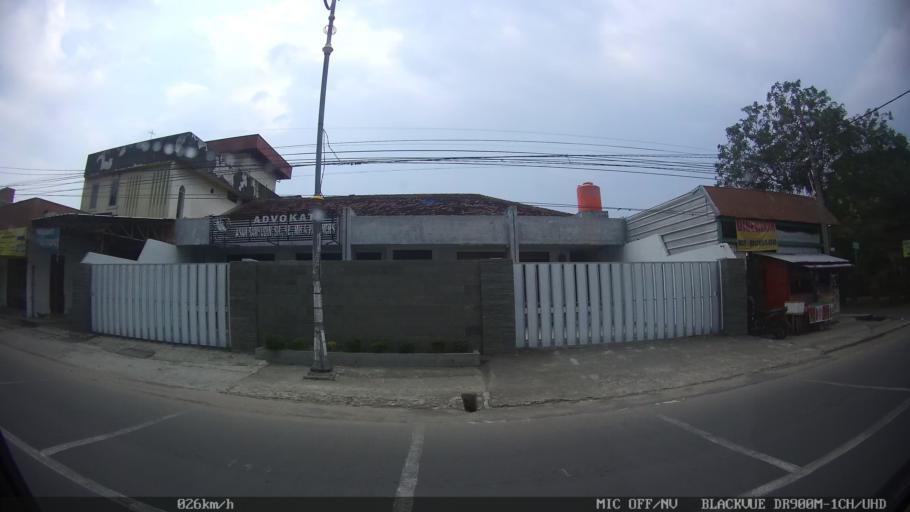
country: ID
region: Lampung
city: Bandarlampung
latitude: -5.4285
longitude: 105.2755
